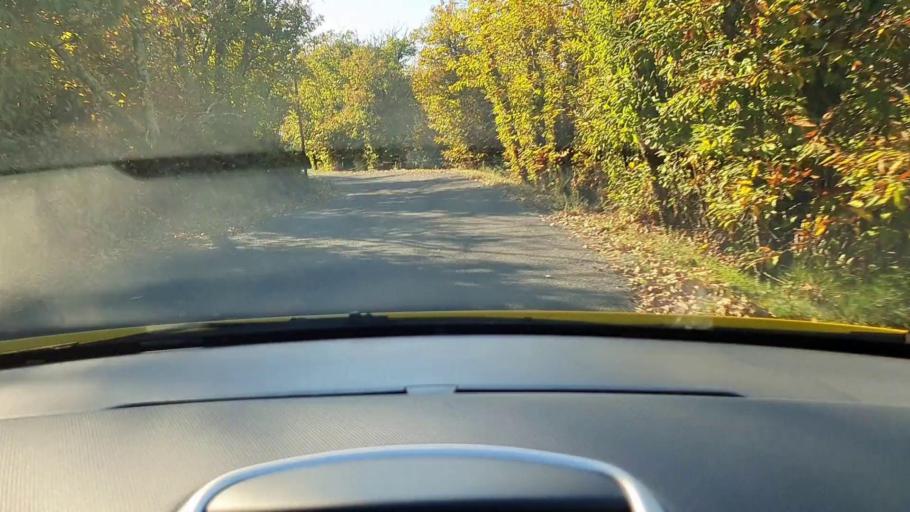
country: FR
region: Languedoc-Roussillon
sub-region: Departement du Gard
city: Sumene
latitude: 44.0373
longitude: 3.7158
